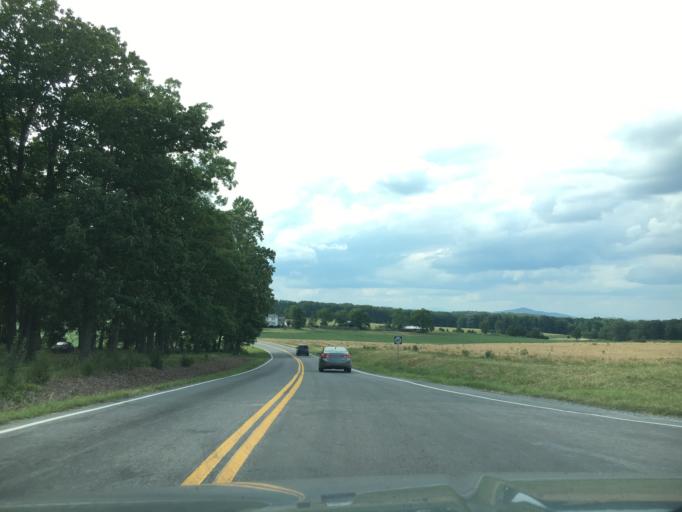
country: US
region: Virginia
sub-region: Campbell County
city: Rustburg
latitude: 37.2623
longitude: -79.1459
